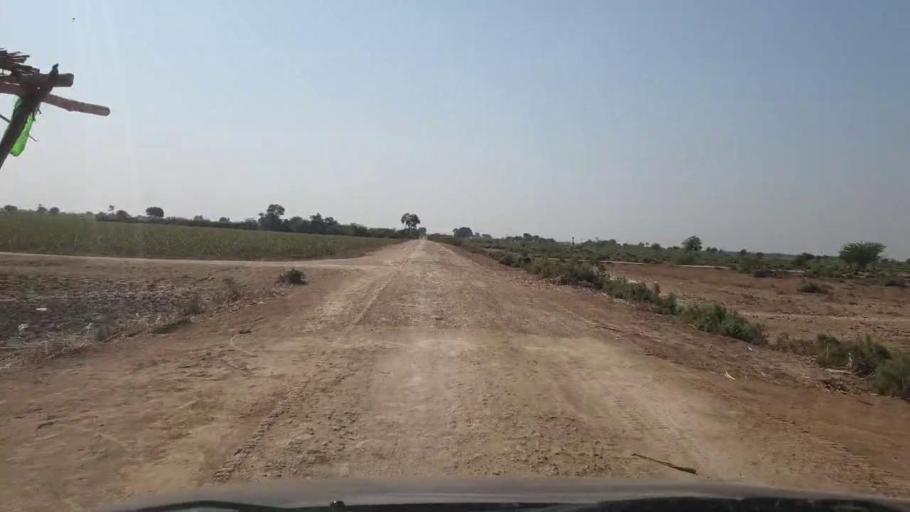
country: PK
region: Sindh
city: Samaro
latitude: 25.2395
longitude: 69.2876
